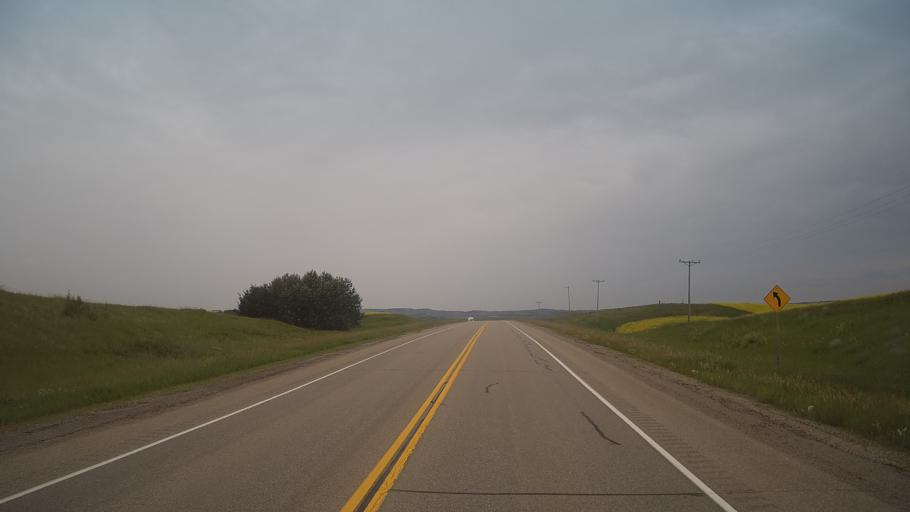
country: CA
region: Saskatchewan
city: Biggar
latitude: 52.0553
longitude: -107.7733
